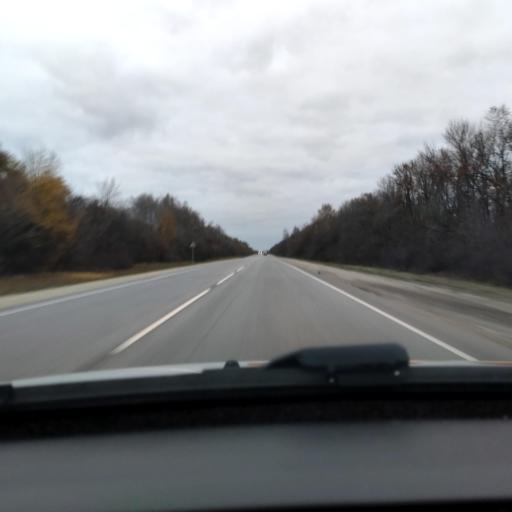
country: RU
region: Lipetsk
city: Borinskoye
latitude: 52.3733
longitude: 39.2116
